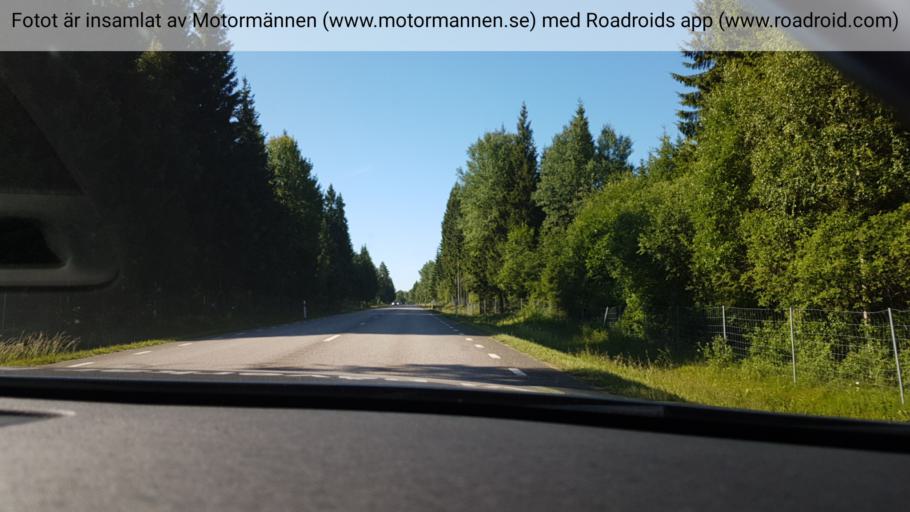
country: SE
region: Vaestra Goetaland
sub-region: Falkopings Kommun
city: Falkoeping
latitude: 58.0390
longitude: 13.5476
